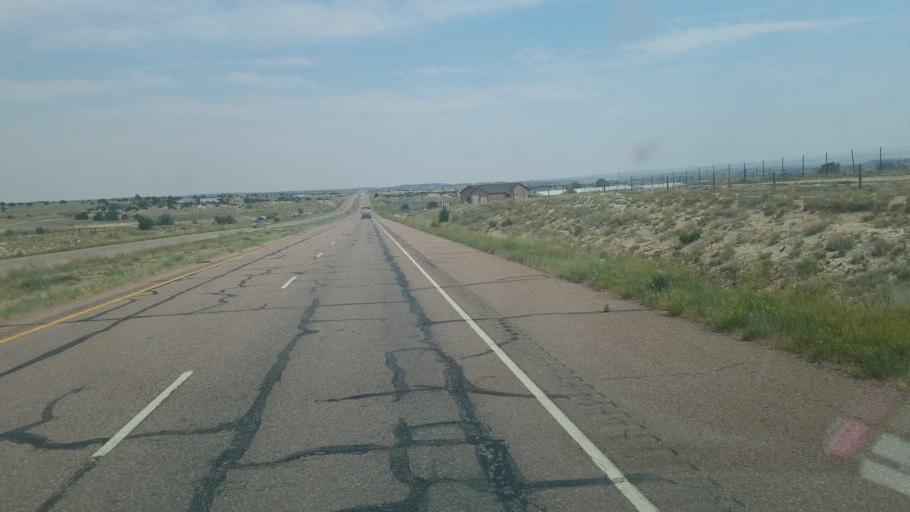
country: US
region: Colorado
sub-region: Fremont County
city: Penrose
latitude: 38.4008
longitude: -104.9812
